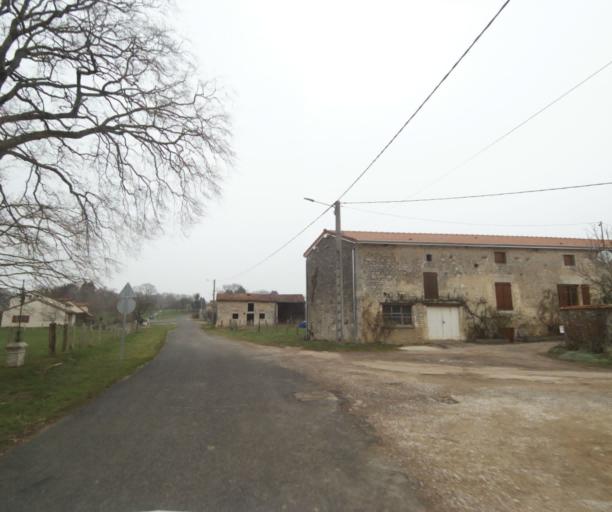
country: FR
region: Champagne-Ardenne
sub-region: Departement de la Haute-Marne
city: Bienville
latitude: 48.5047
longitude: 5.0376
